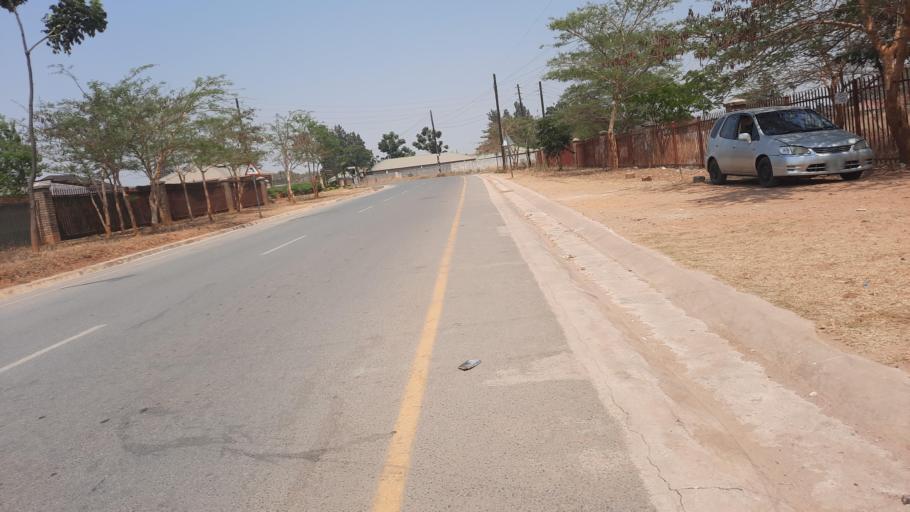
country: ZM
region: Lusaka
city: Lusaka
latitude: -15.3938
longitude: 28.3945
